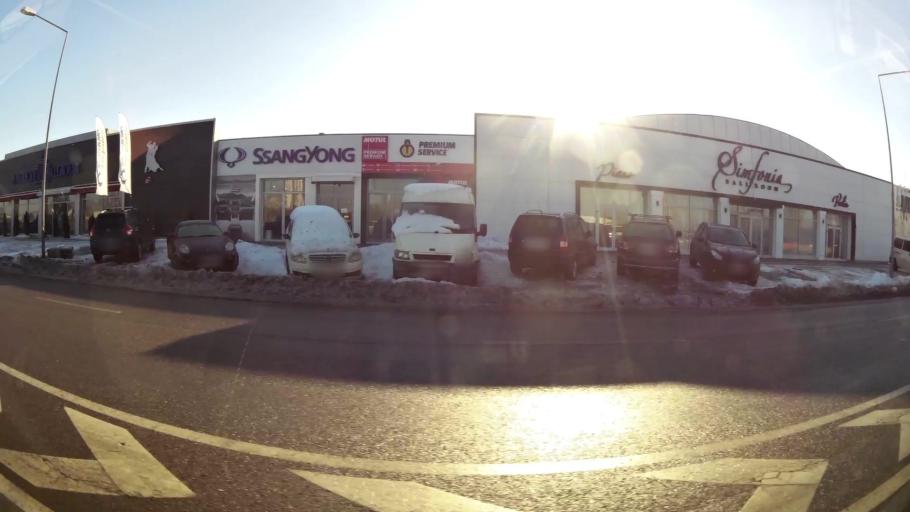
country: RO
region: Bucuresti
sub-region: Municipiul Bucuresti
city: Bucharest
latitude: 44.4853
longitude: 26.1122
